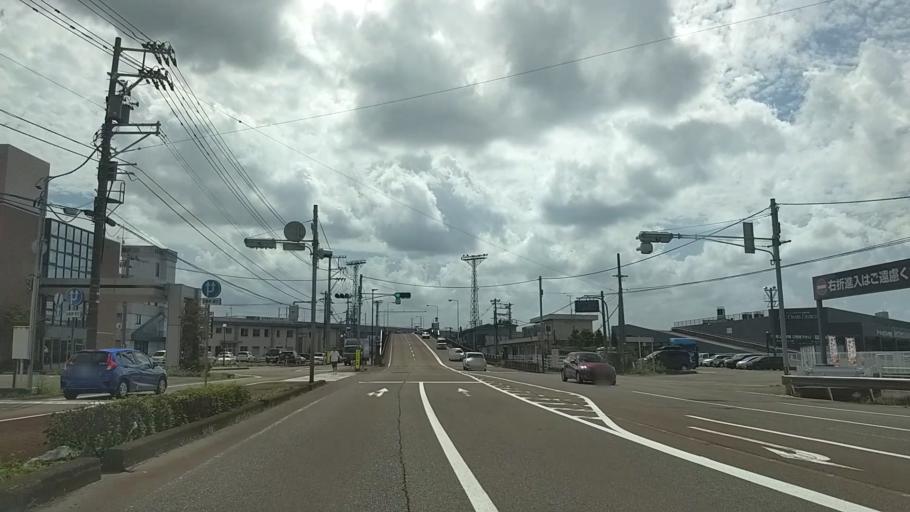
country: JP
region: Ishikawa
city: Kanazawa-shi
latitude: 36.5918
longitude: 136.6634
